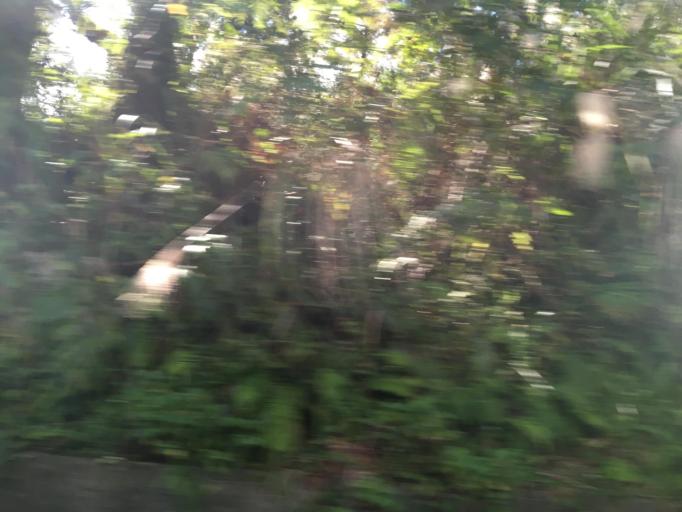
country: TW
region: Taiwan
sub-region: Yilan
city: Yilan
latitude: 24.7531
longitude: 121.6319
